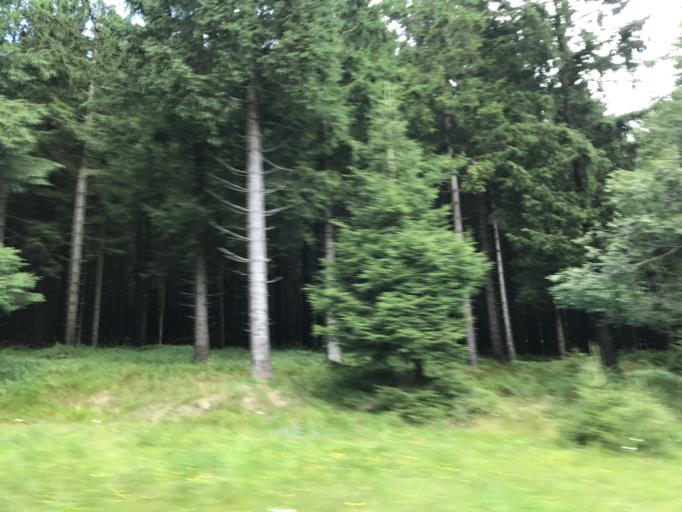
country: DE
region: Lower Saxony
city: Sankt Andreasberg
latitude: 51.7404
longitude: 10.5208
